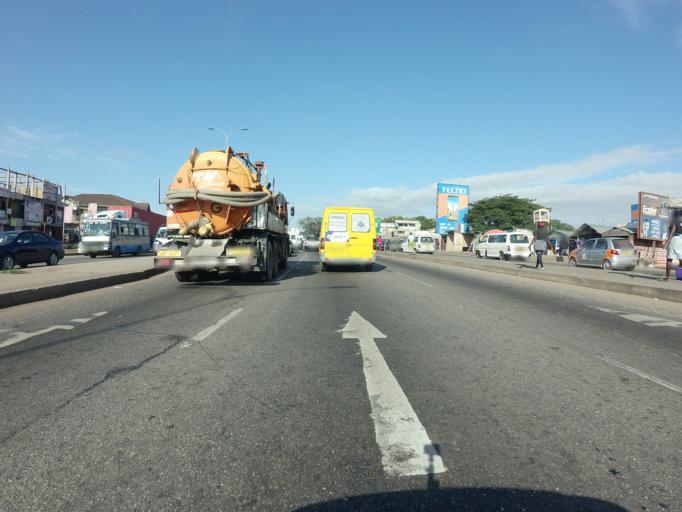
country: GH
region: Greater Accra
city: Gbawe
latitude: 5.5805
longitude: -0.2626
